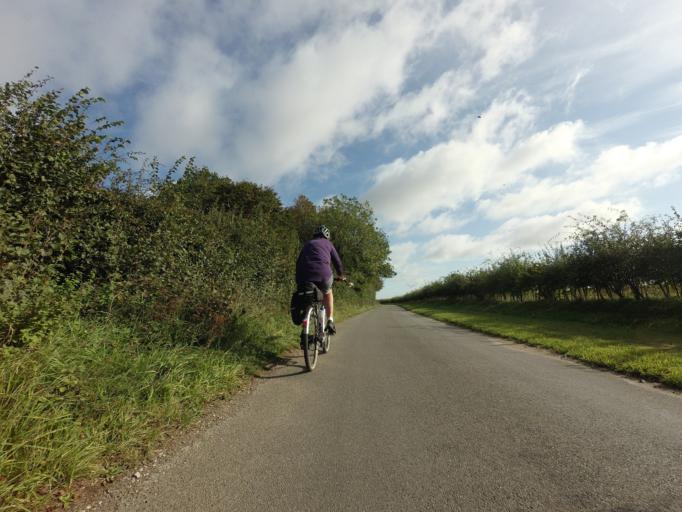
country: GB
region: England
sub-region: Norfolk
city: Fakenham
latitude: 52.8830
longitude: 0.6826
